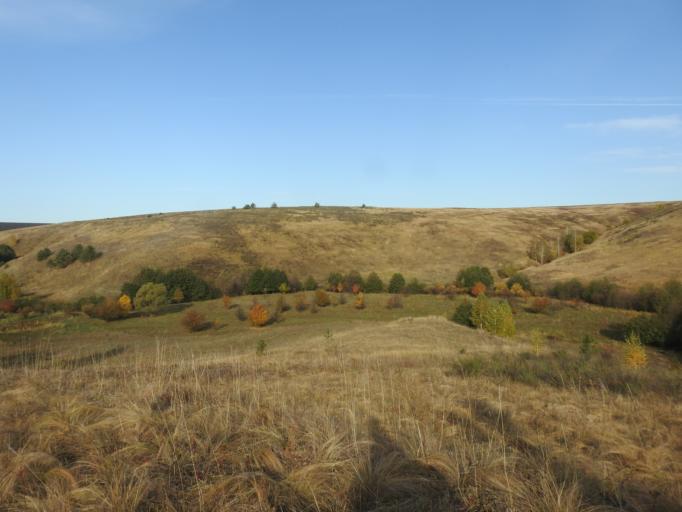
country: RU
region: Saratov
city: Baltay
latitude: 52.5650
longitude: 46.6726
